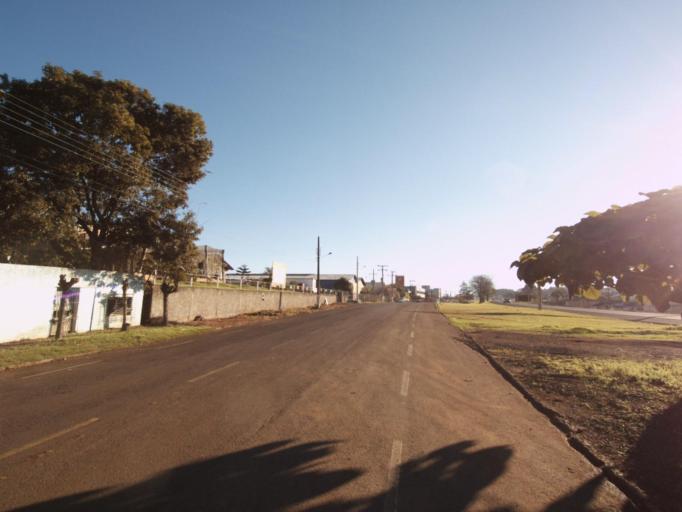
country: BR
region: Santa Catarina
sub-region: Chapeco
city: Chapeco
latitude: -26.9057
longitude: -52.8997
